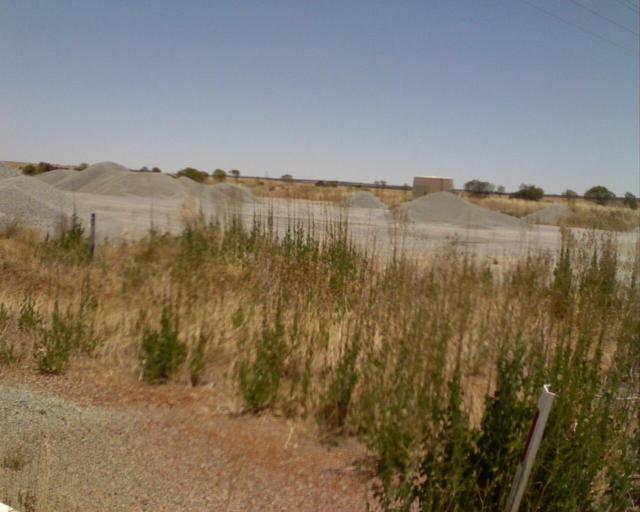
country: AU
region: Western Australia
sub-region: Merredin
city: Merredin
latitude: -30.8330
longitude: 117.8623
